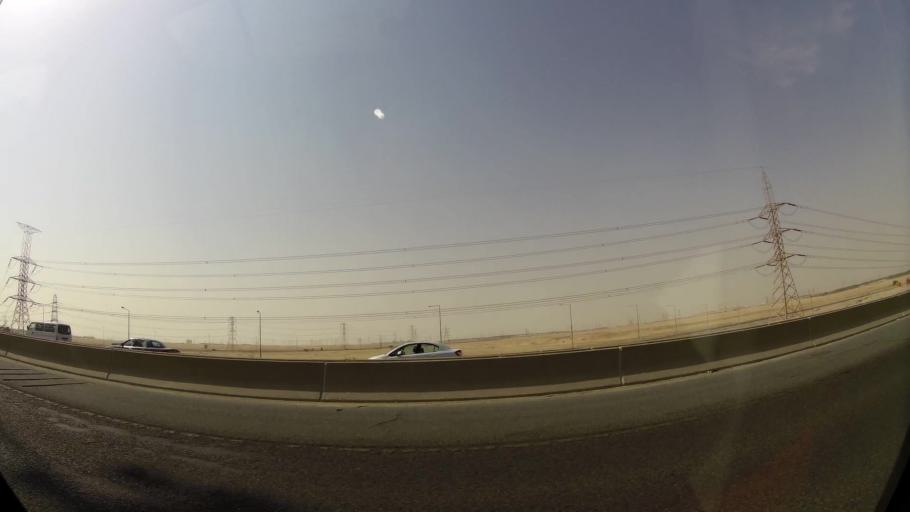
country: KW
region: Al Ahmadi
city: Al Fahahil
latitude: 29.0409
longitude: 48.1163
